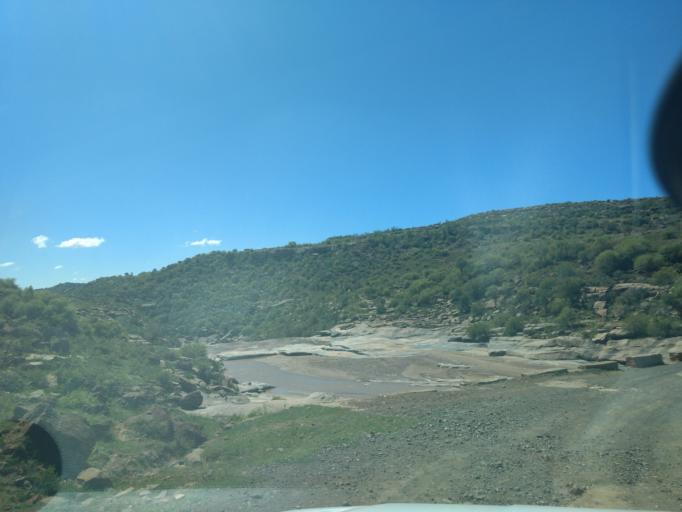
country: LS
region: Maseru
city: Maseru
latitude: -29.4831
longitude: 27.3704
